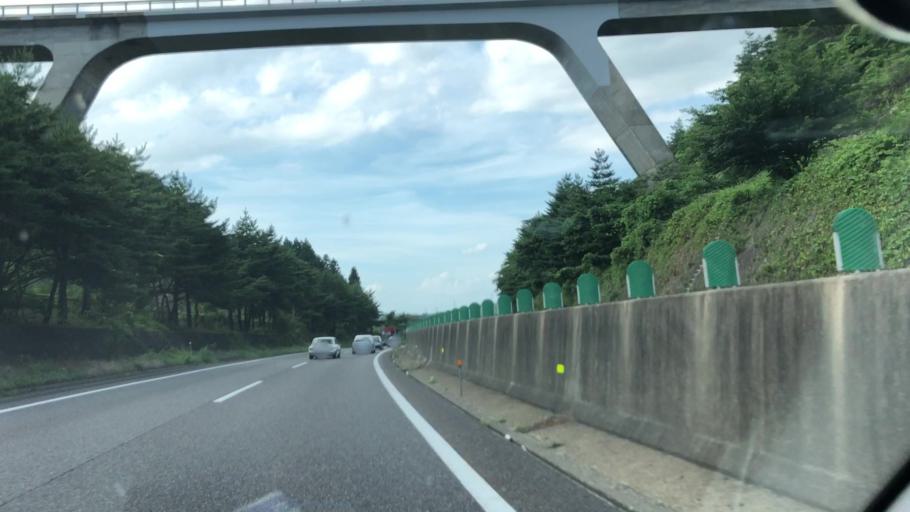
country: JP
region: Fukushima
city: Nihommatsu
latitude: 37.6353
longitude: 140.4337
